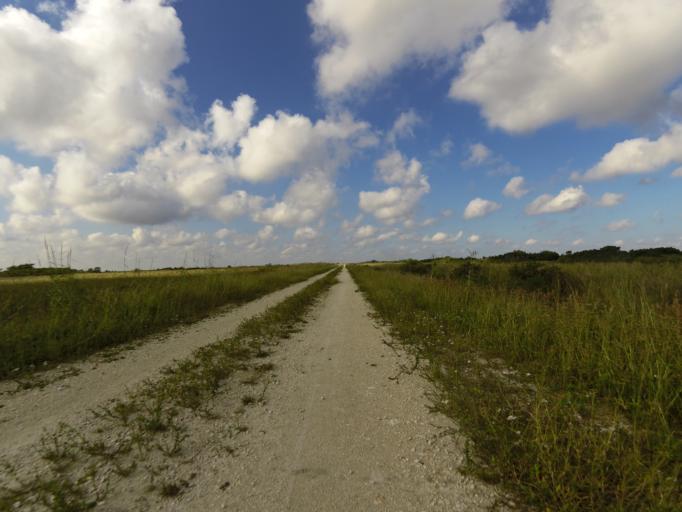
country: US
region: Florida
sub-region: Broward County
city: Weston
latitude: 26.0555
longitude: -80.4590
